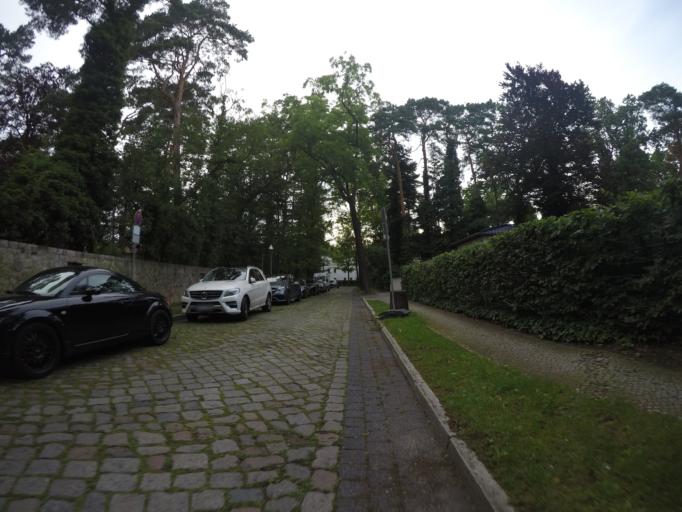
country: DE
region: Berlin
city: Dahlem
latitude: 52.4642
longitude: 13.2863
